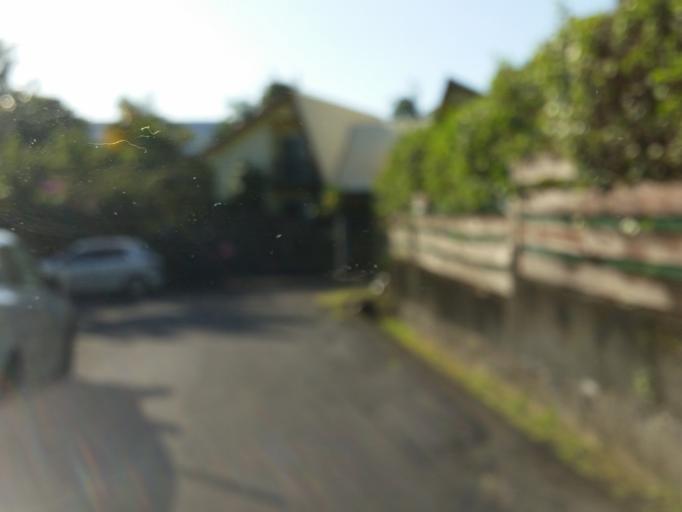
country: RE
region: Reunion
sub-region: Reunion
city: Sainte-Marie
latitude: -20.9158
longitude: 55.5122
